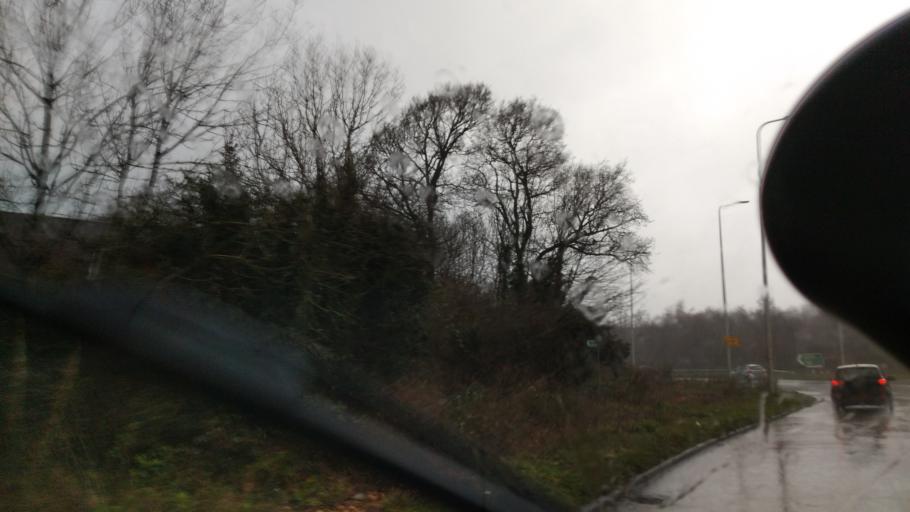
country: GB
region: England
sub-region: West Sussex
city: Fontwell
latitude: 50.8562
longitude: -0.6419
